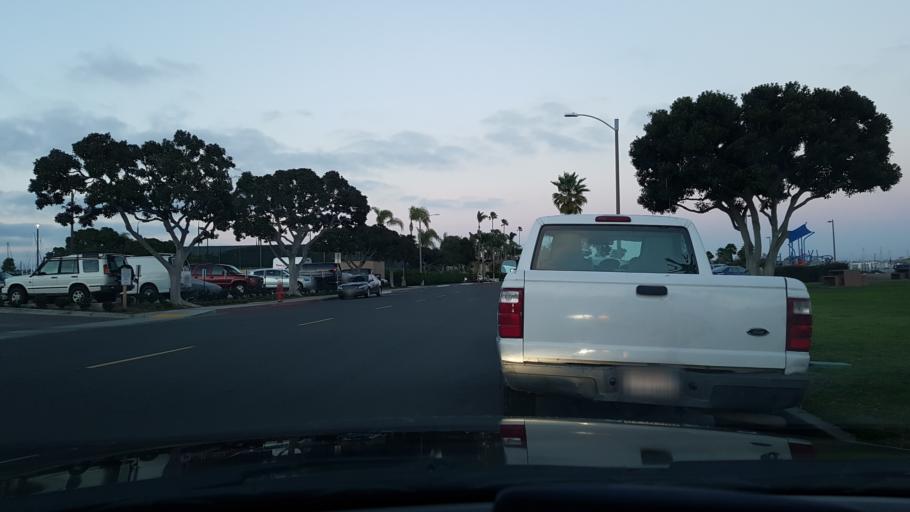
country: US
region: California
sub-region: San Diego County
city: Coronado
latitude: 32.7107
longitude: -117.2301
